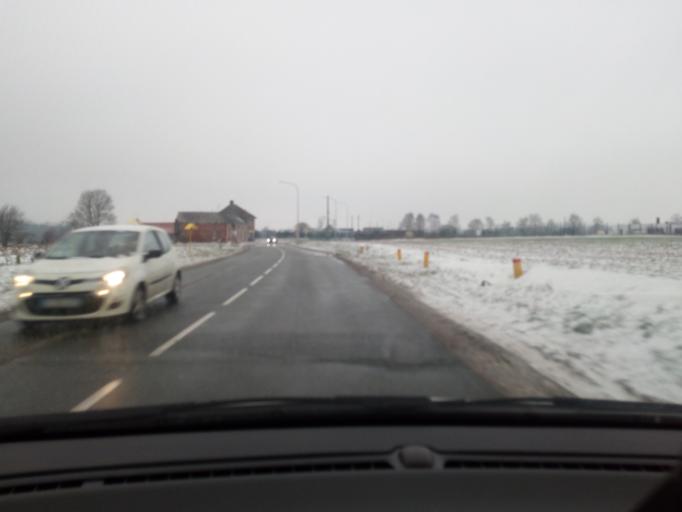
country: FR
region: Nord-Pas-de-Calais
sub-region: Departement du Nord
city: La Longueville
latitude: 50.3370
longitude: 3.8737
